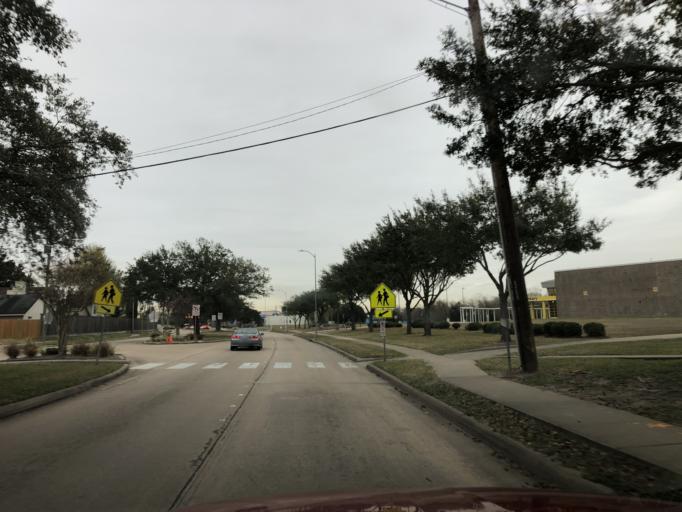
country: US
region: Texas
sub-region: Fort Bend County
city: Missouri City
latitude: 29.6390
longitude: -95.5290
